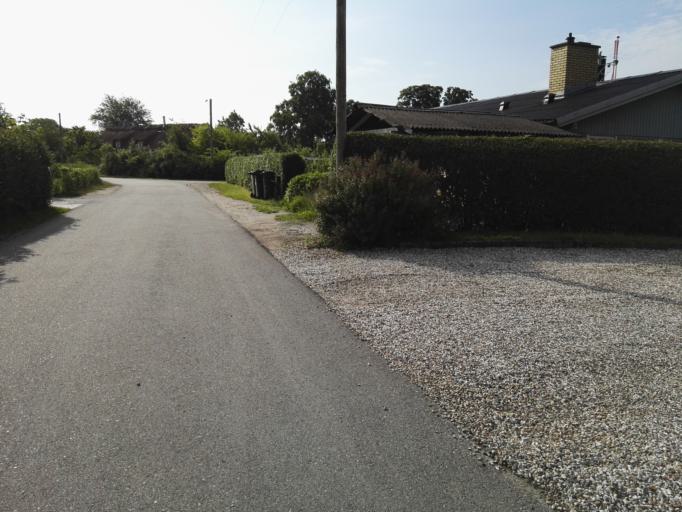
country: DK
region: Zealand
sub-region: Roskilde Kommune
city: Jyllinge
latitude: 55.7979
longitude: 12.1111
